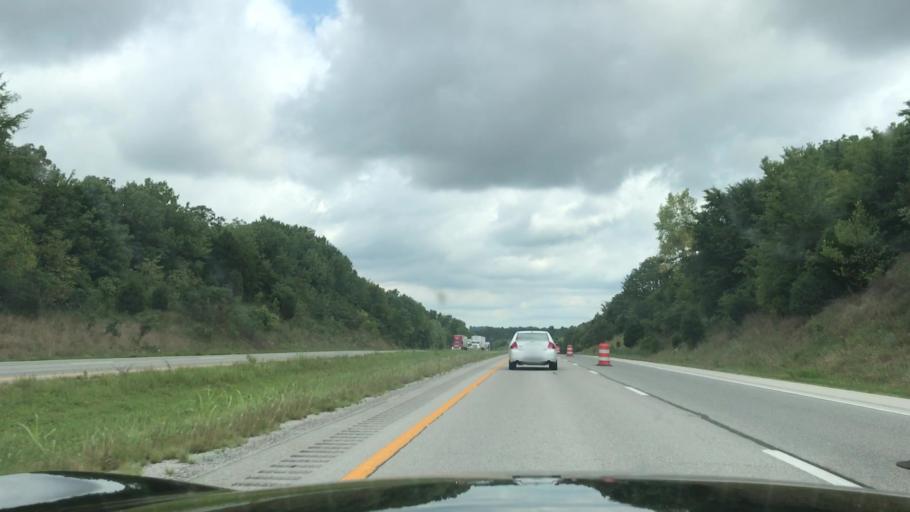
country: US
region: Kentucky
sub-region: Butler County
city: Morgantown
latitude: 37.1131
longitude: -86.6411
